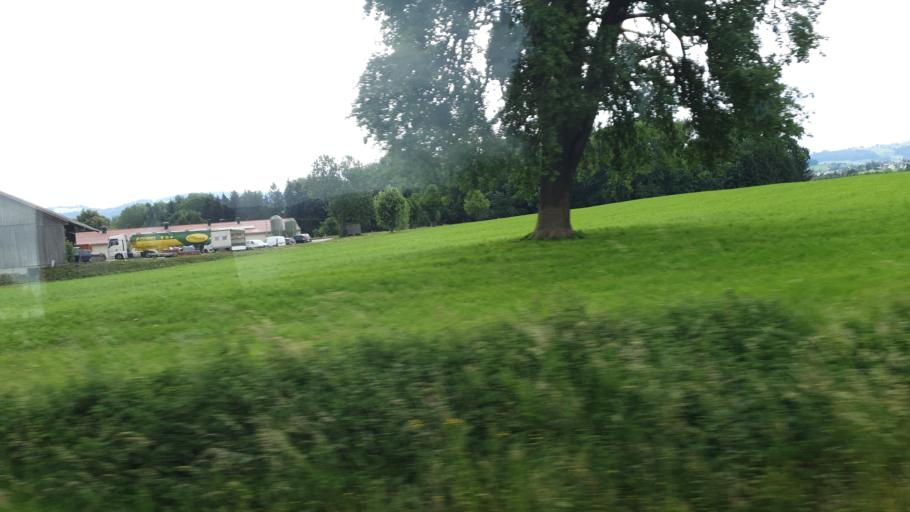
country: CH
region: Saint Gallen
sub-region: Wahlkreis Rorschach
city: Morschwil
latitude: 47.4763
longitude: 9.4313
